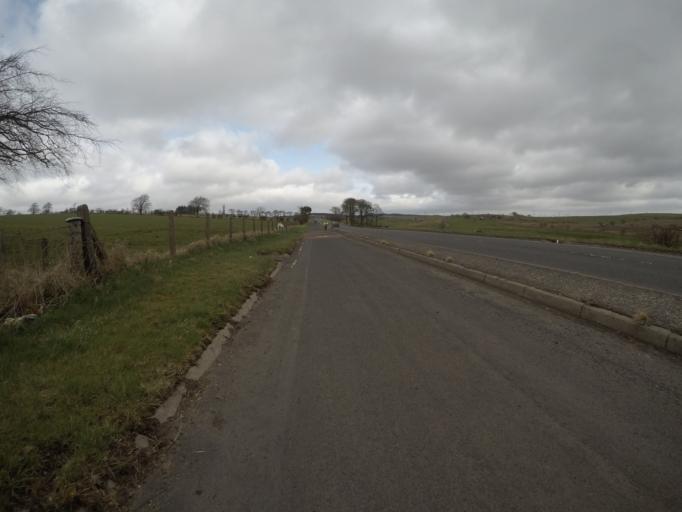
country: GB
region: Scotland
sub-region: East Ayrshire
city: Galston
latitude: 55.6843
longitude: -4.4181
